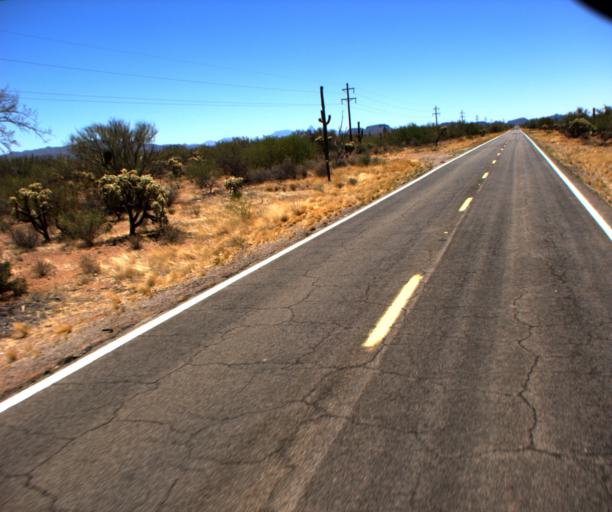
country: US
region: Arizona
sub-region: Pima County
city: Sells
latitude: 32.0511
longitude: -112.0262
